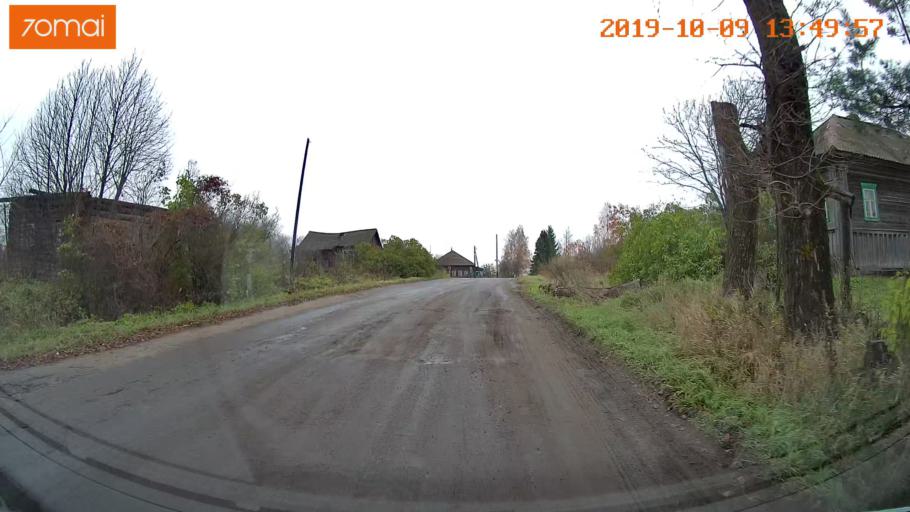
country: RU
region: Kostroma
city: Buy
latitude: 58.4024
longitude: 41.2393
